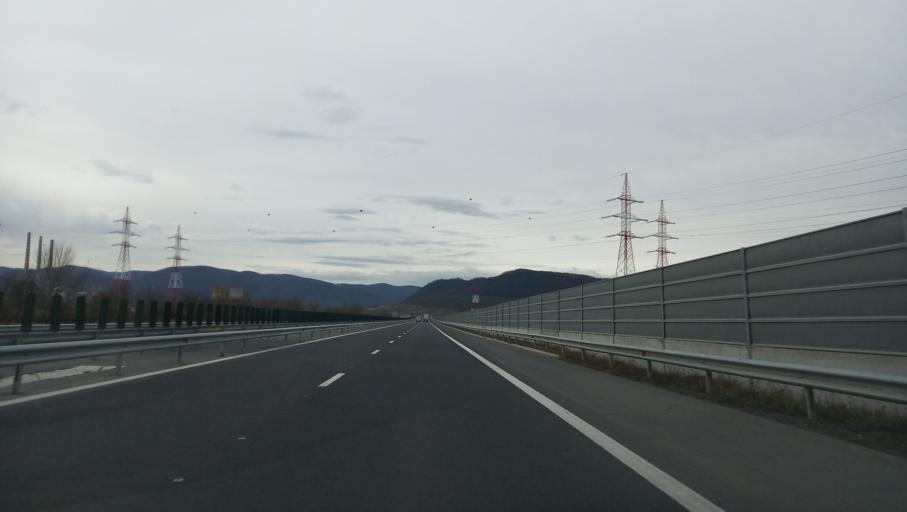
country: RO
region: Hunedoara
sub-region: Comuna Vetel
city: Vetel
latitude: 45.9295
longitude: 22.8467
